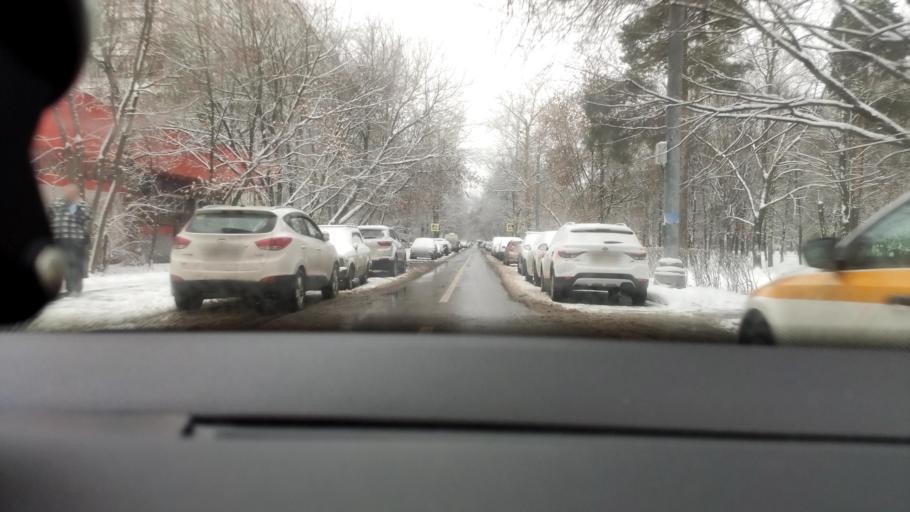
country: RU
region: Moscow
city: Leonovo
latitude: 55.8623
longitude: 37.6684
